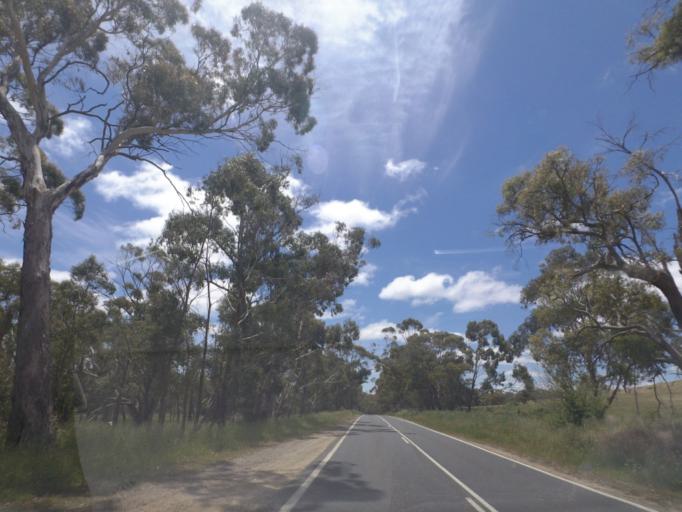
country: AU
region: Victoria
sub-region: Mount Alexander
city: Castlemaine
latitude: -37.3192
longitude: 144.1639
